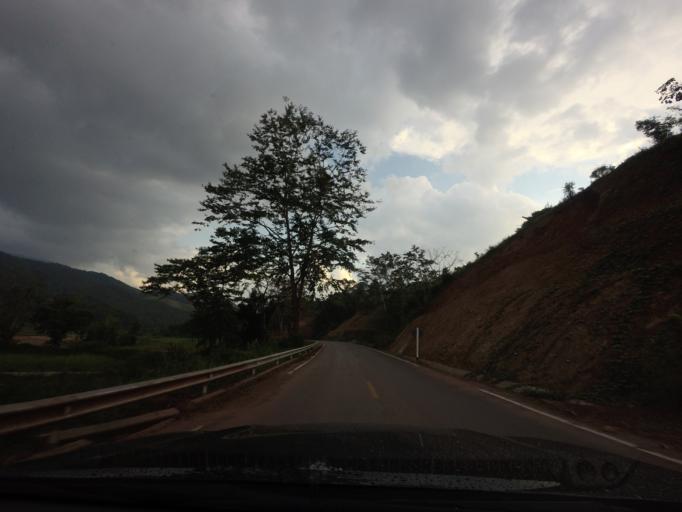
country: TH
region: Nan
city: Bo Kluea
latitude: 19.2204
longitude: 101.1832
